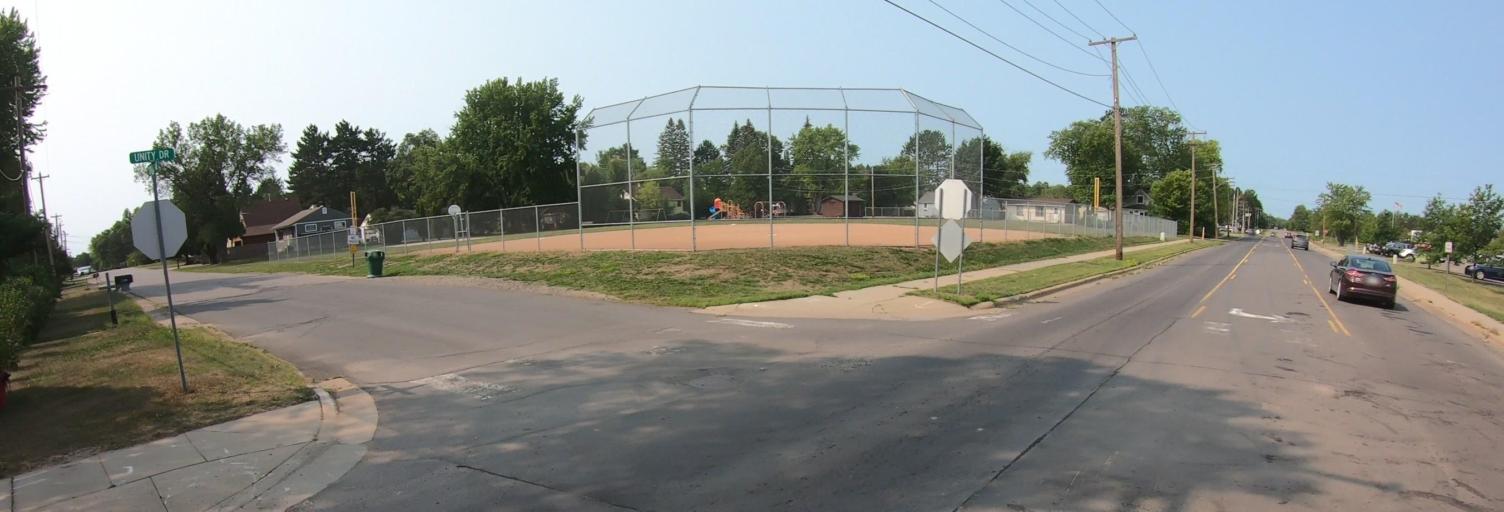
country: US
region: Minnesota
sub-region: Saint Louis County
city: Parkville
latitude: 47.5174
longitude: -92.5675
